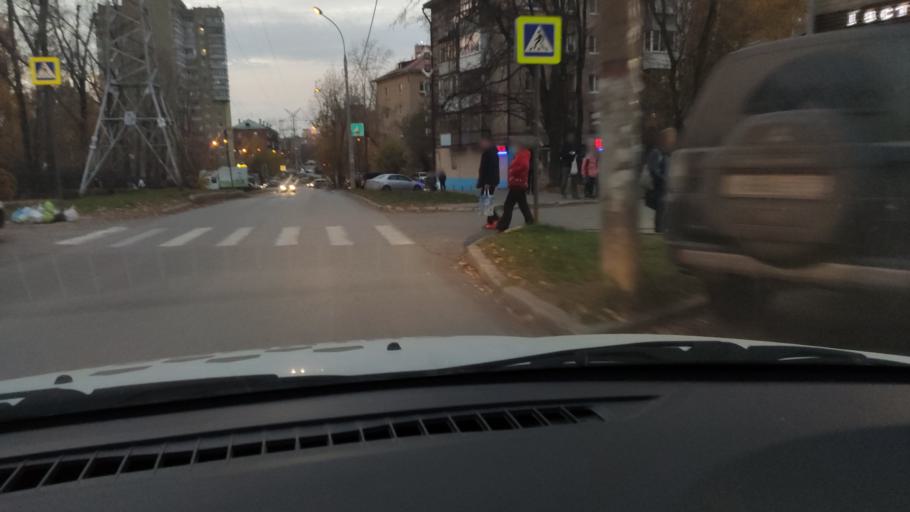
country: RU
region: Perm
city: Perm
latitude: 57.9823
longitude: 56.2105
